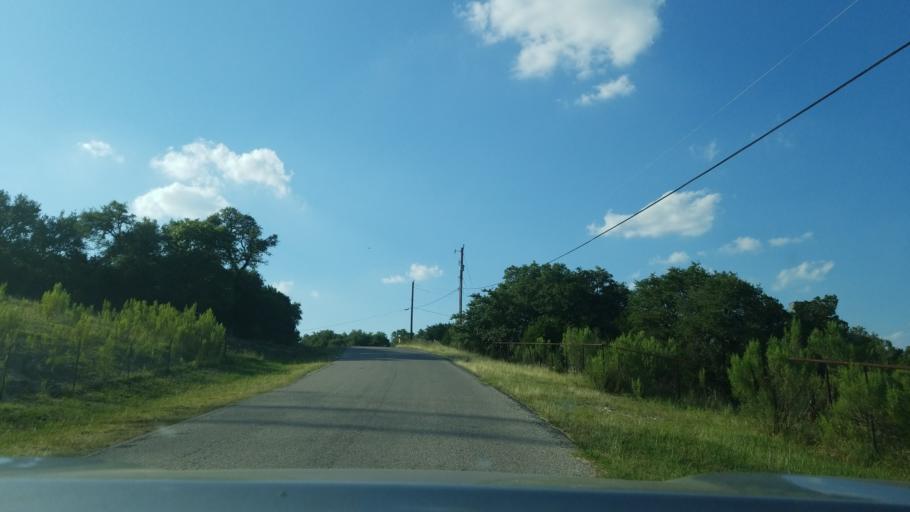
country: US
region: Texas
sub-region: Comal County
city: Bulverde
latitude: 29.7787
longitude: -98.4306
